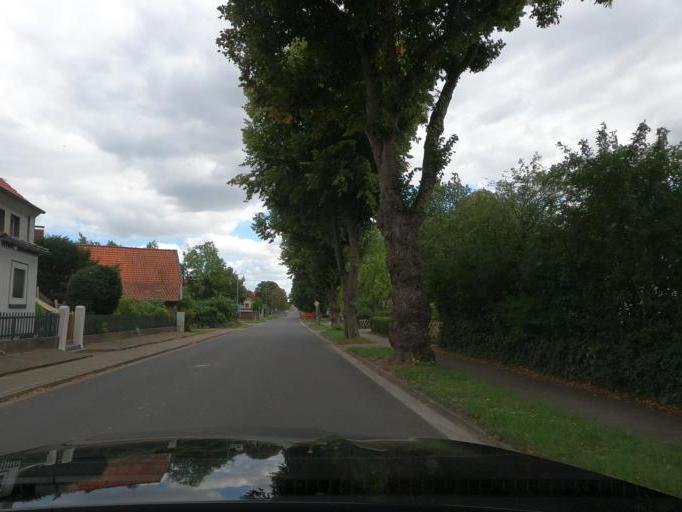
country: DE
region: Lower Saxony
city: Ilsede
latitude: 52.2486
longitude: 10.1606
